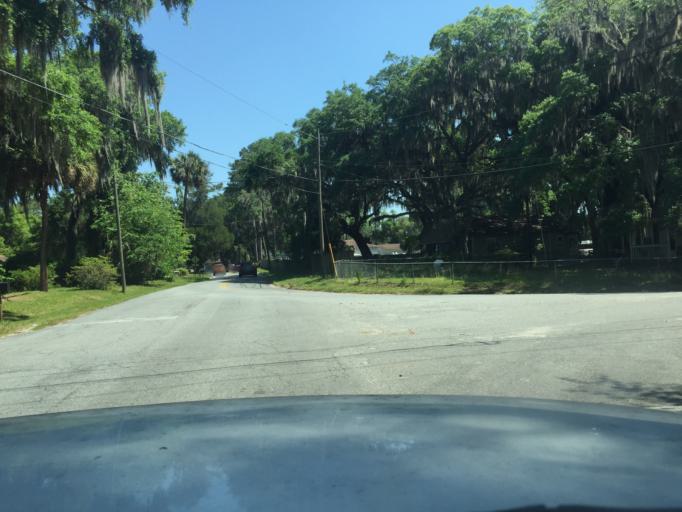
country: US
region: Georgia
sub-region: Chatham County
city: Montgomery
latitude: 31.9387
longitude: -81.1077
